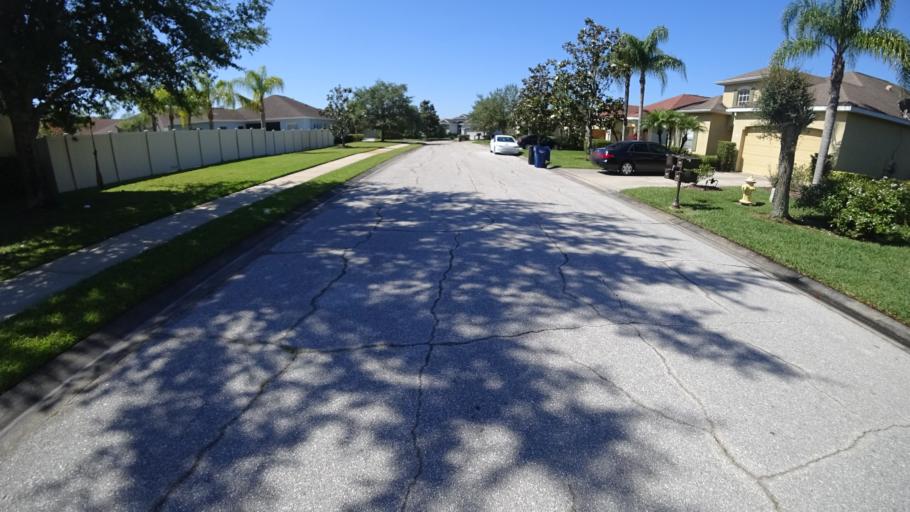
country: US
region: Florida
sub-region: Manatee County
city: Ellenton
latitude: 27.5647
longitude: -82.4443
